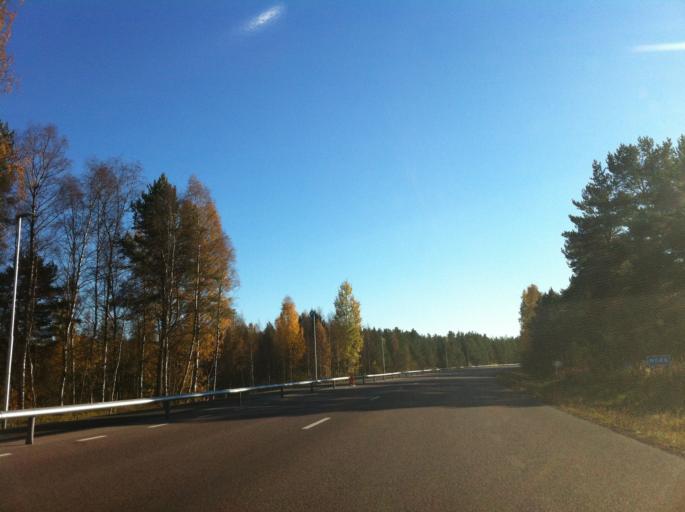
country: SE
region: Dalarna
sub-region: Mora Kommun
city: Mora
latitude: 61.0241
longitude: 14.5343
